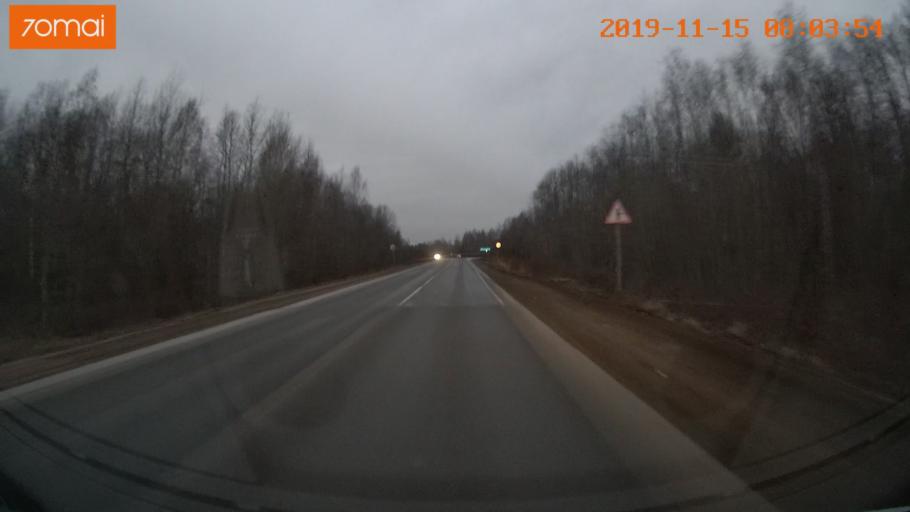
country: RU
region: Vologda
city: Cherepovets
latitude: 59.0029
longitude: 38.0833
